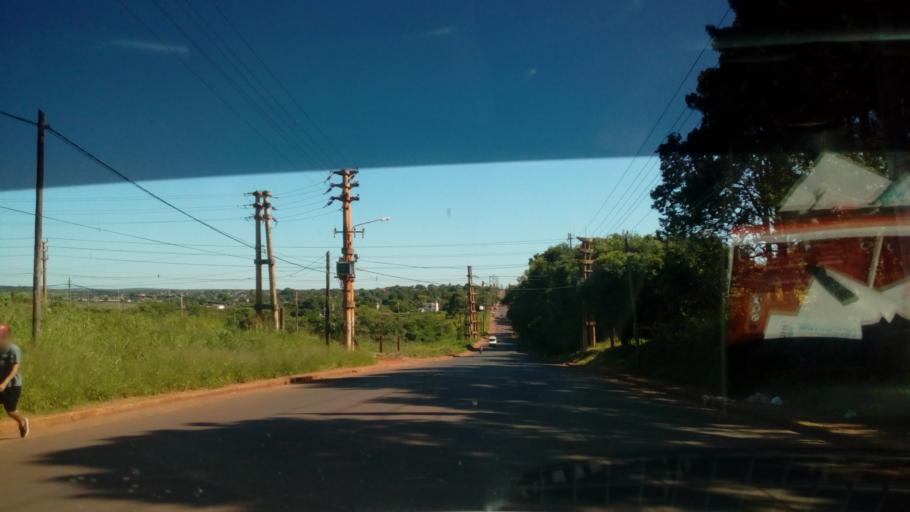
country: AR
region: Misiones
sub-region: Departamento de Capital
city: Posadas
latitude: -27.4172
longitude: -55.9128
